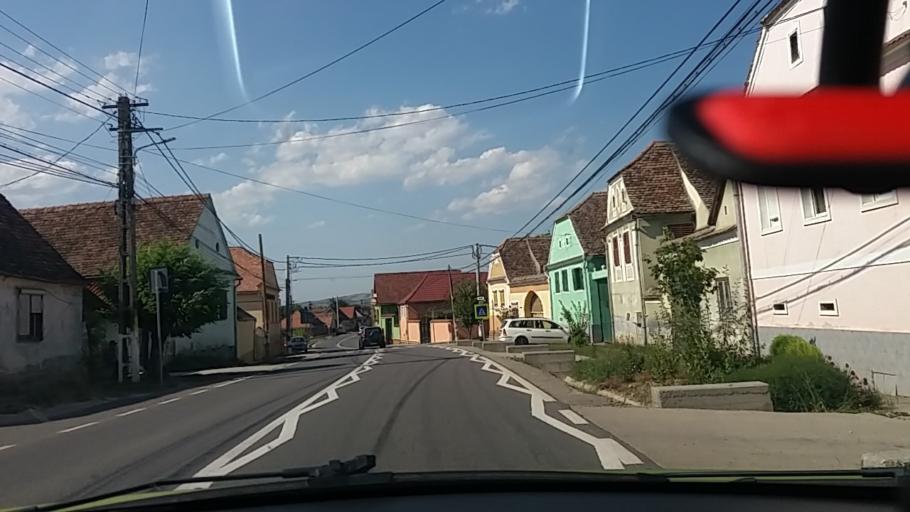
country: RO
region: Sibiu
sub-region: Comuna Slimnic
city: Slimnic
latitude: 45.9583
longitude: 24.1666
